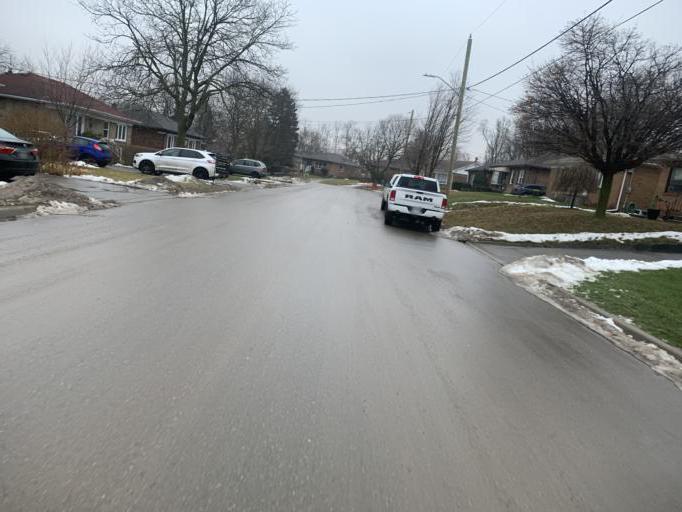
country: CA
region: Ontario
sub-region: Halton
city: Milton
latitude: 43.6549
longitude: -79.9292
